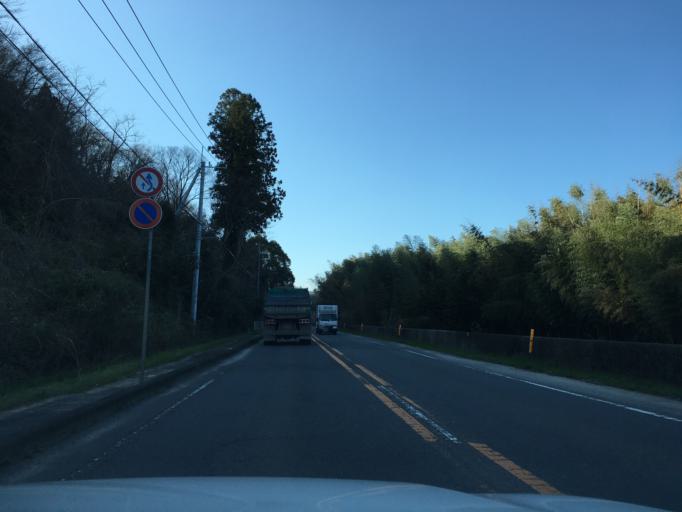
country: JP
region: Ibaraki
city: Omiya
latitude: 36.5988
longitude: 140.4055
